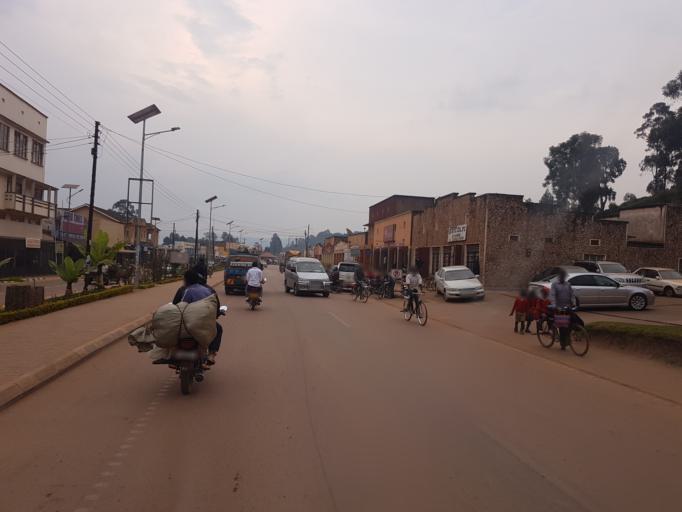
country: UG
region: Western Region
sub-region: Kabale District
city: Kabale
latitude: -1.2514
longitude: 29.9865
